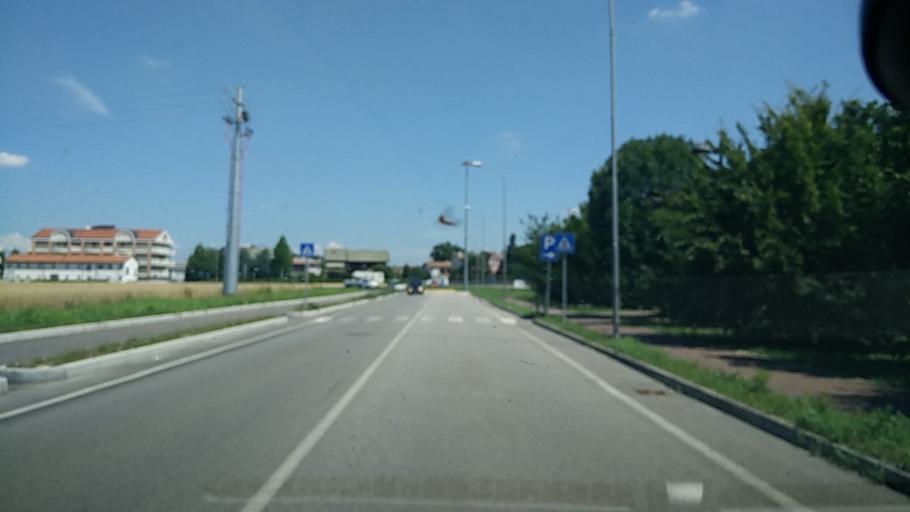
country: IT
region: Veneto
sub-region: Provincia di Venezia
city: Marcon-Gaggio-Colmello
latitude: 45.5537
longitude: 12.2931
